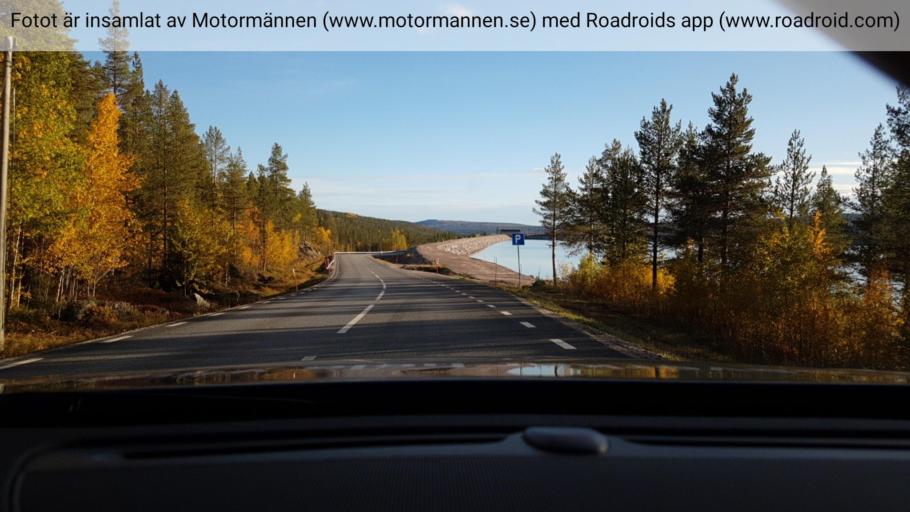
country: SE
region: Norrbotten
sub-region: Jokkmokks Kommun
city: Jokkmokk
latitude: 66.8923
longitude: 19.8274
